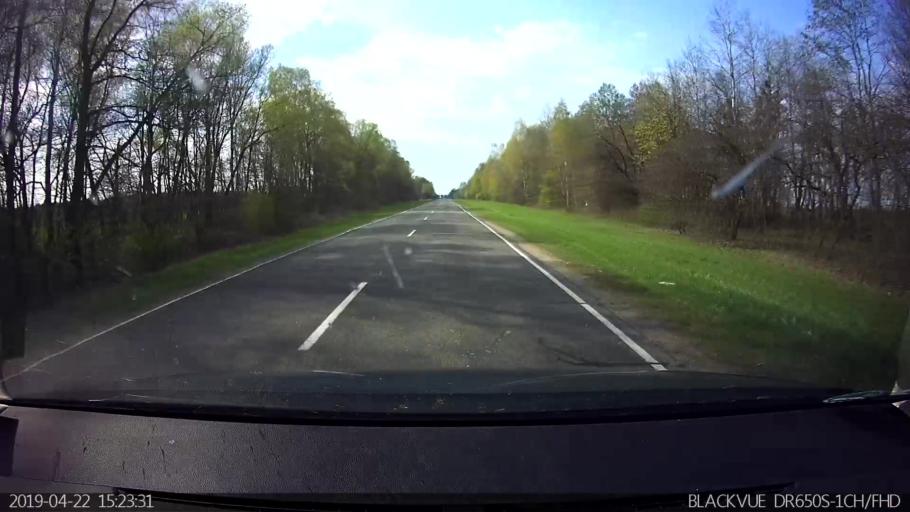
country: BY
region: Brest
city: Vysokaye
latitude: 52.3556
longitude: 23.4250
